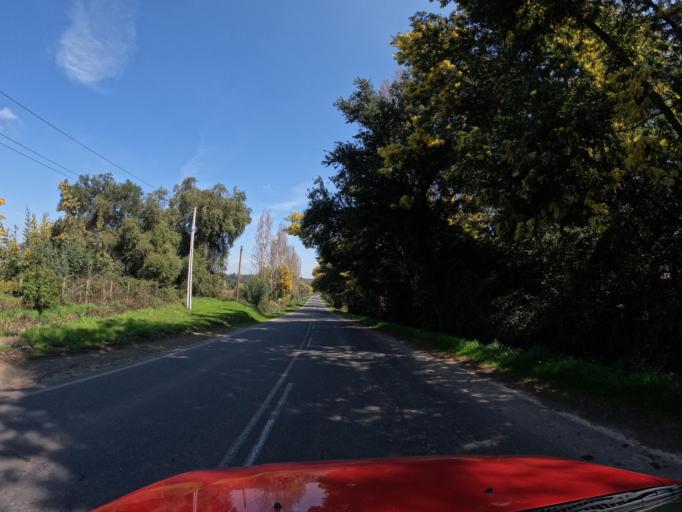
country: CL
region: Maule
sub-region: Provincia de Talca
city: San Clemente
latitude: -35.4867
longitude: -71.2911
